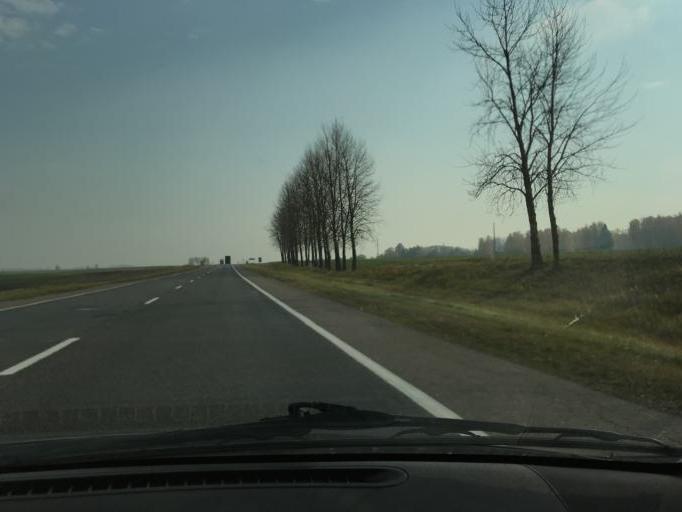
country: BY
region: Vitebsk
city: Chashniki
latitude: 55.0169
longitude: 29.0418
